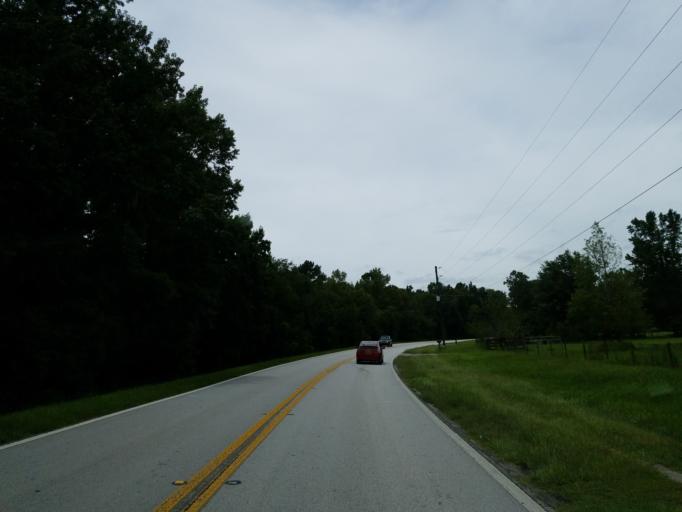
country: US
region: Florida
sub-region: Sumter County
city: Bushnell
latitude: 28.6692
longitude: -82.1850
